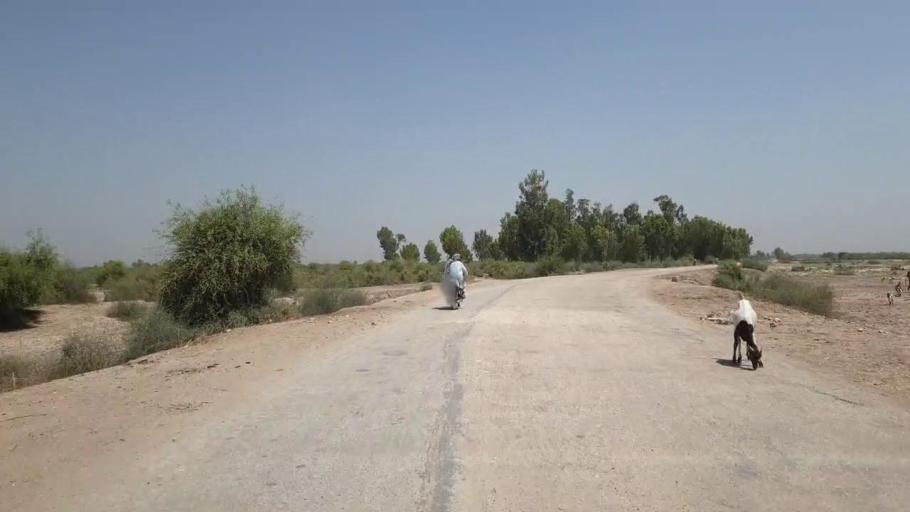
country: PK
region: Sindh
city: Adilpur
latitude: 27.8947
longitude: 69.2892
